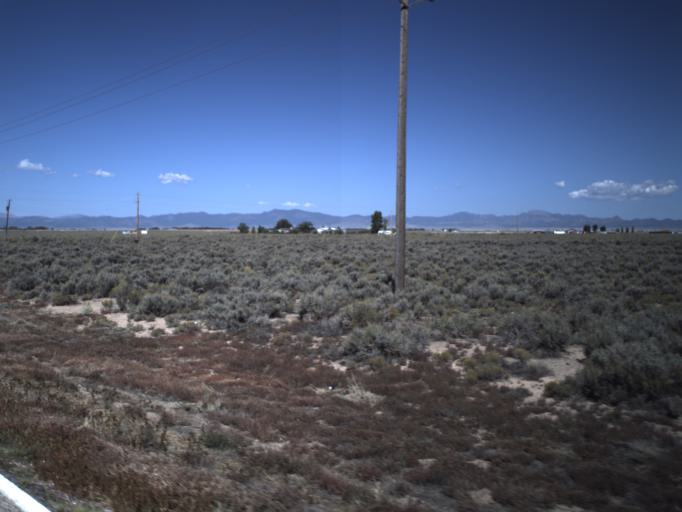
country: US
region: Utah
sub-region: Washington County
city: Enterprise
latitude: 37.6976
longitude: -113.6232
